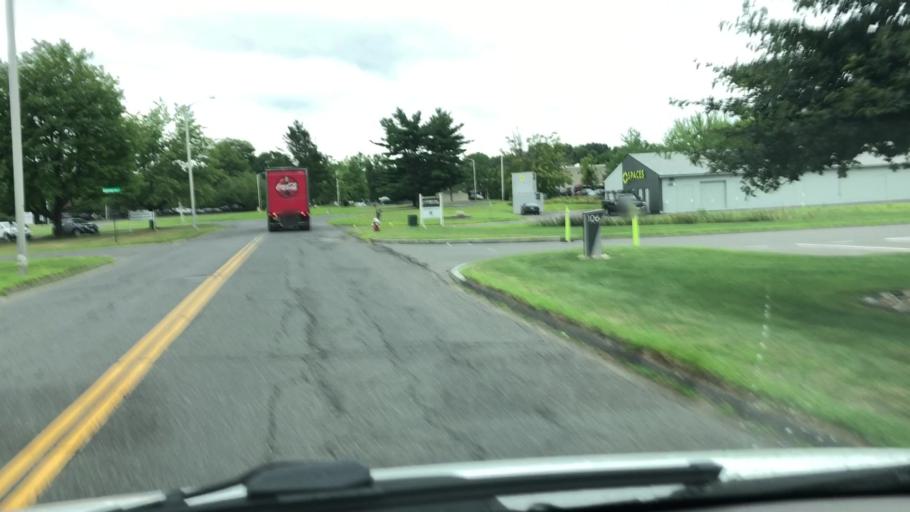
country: US
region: Massachusetts
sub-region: Hampshire County
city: Northampton
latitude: 42.3352
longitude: -72.6310
